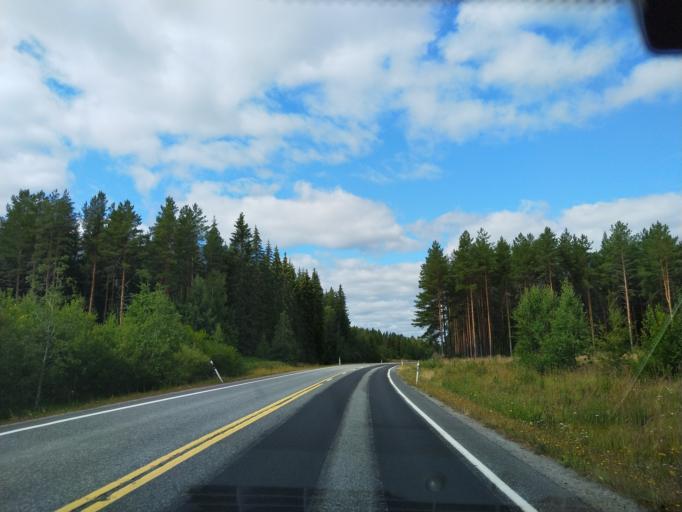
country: FI
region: Haeme
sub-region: Haemeenlinna
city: Tervakoski
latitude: 60.7417
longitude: 24.6756
